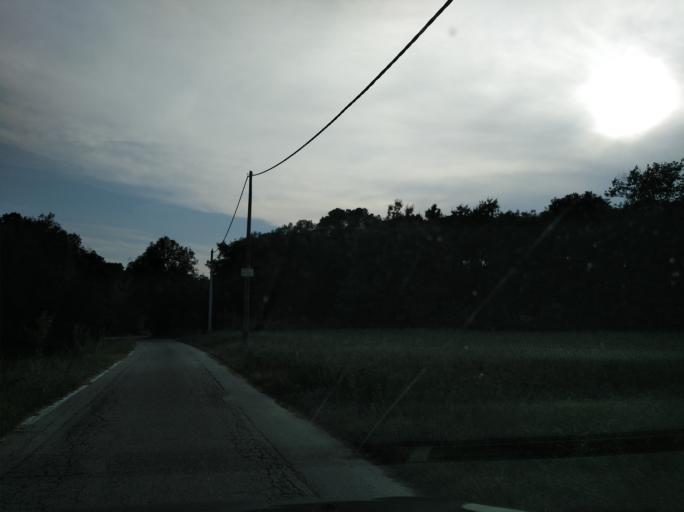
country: ES
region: Catalonia
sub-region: Provincia de Girona
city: Aiguaviva
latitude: 41.9406
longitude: 2.7701
